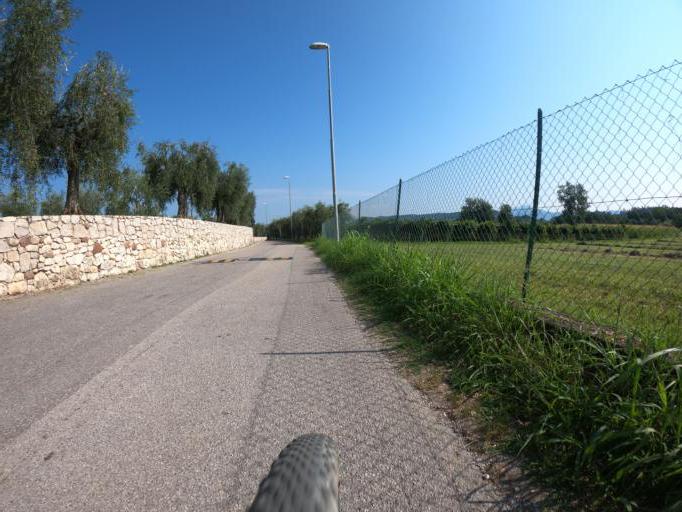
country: IT
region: Veneto
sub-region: Provincia di Verona
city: Calmasino
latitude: 45.5236
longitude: 10.7358
